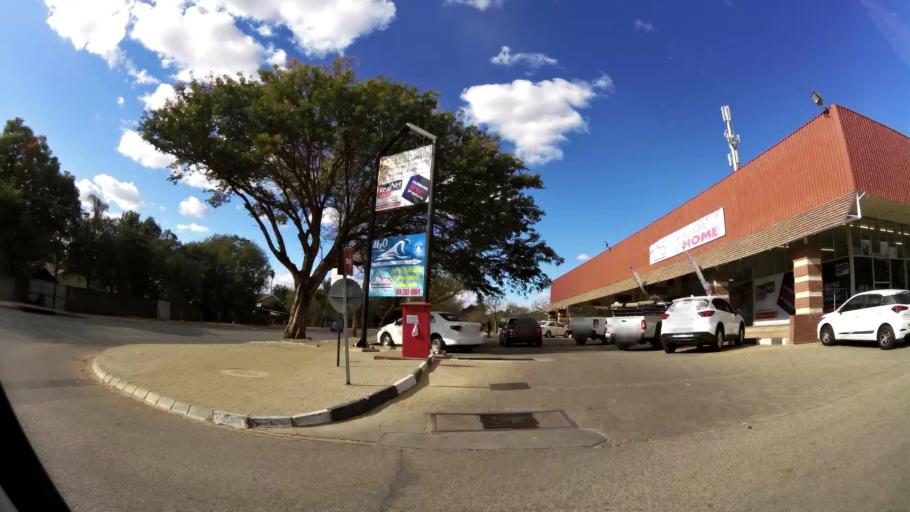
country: ZA
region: Limpopo
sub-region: Capricorn District Municipality
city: Polokwane
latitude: -23.8940
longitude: 29.4693
